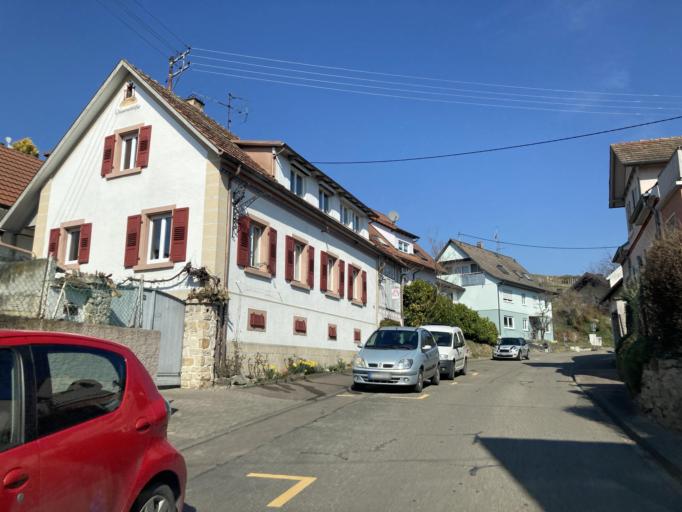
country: DE
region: Baden-Wuerttemberg
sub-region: Freiburg Region
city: Ihringen
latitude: 48.0470
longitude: 7.6445
